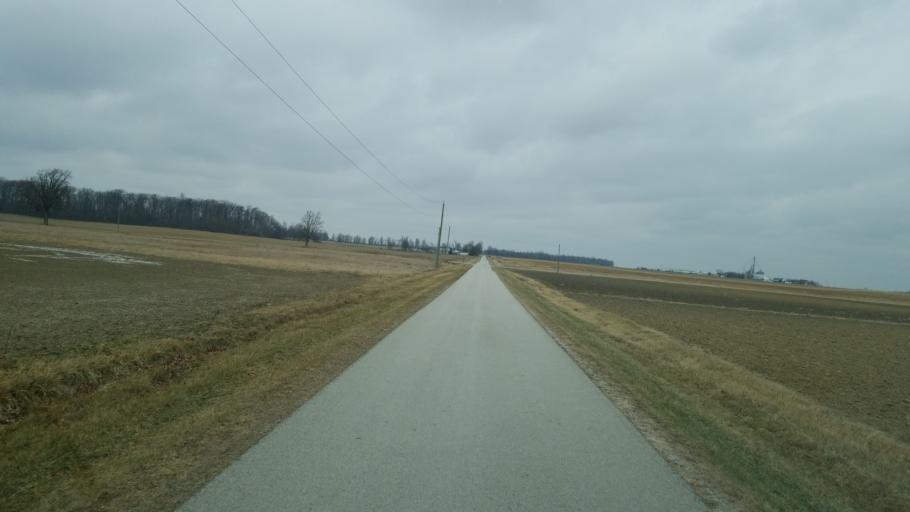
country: US
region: Ohio
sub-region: Hardin County
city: Forest
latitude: 40.7726
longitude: -83.4777
